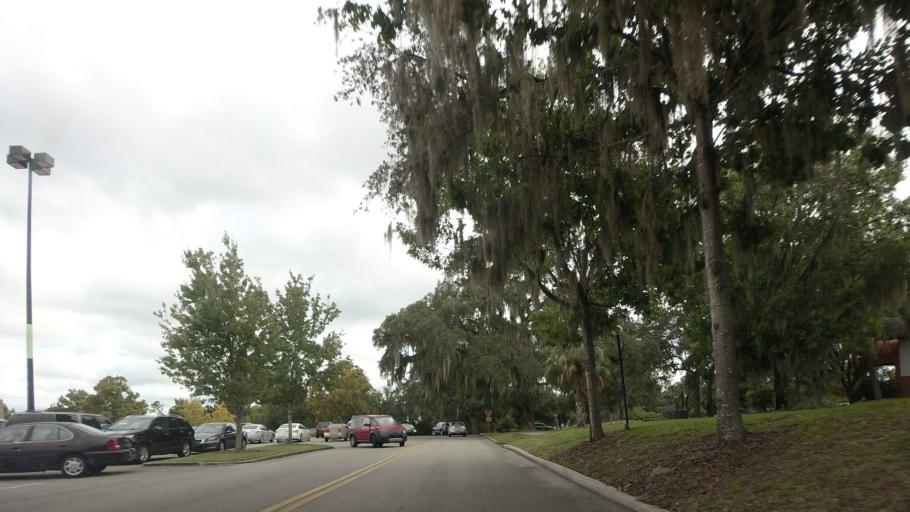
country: US
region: Florida
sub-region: Alachua County
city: Gainesville
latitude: 29.6570
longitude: -82.4138
